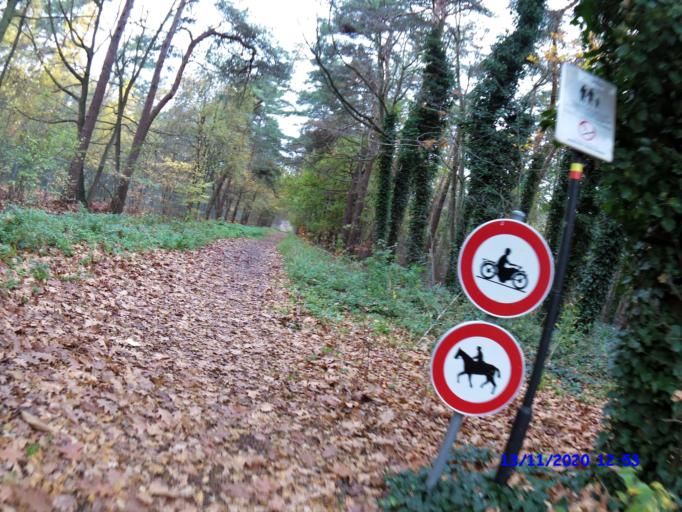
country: BE
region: Flanders
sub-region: Provincie Antwerpen
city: Mol
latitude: 51.1974
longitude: 5.0510
